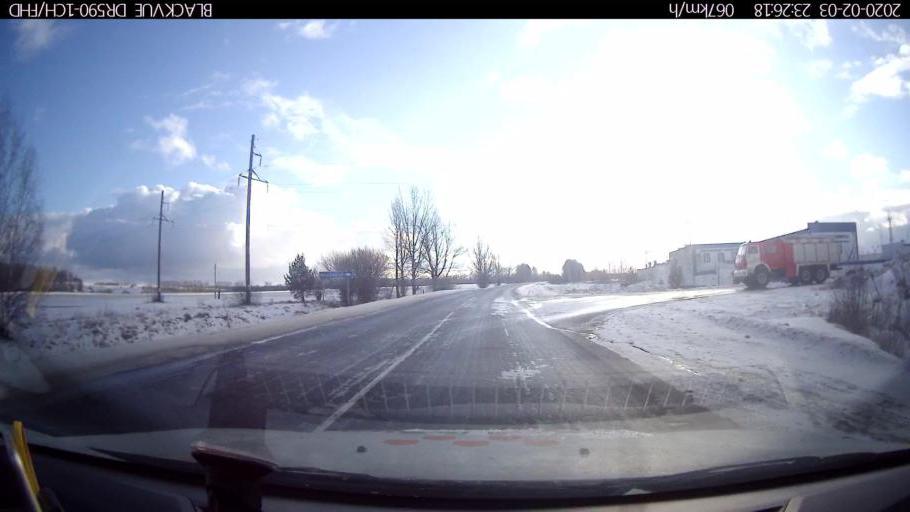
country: RU
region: Nizjnij Novgorod
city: Kstovo
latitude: 55.9943
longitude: 44.2130
